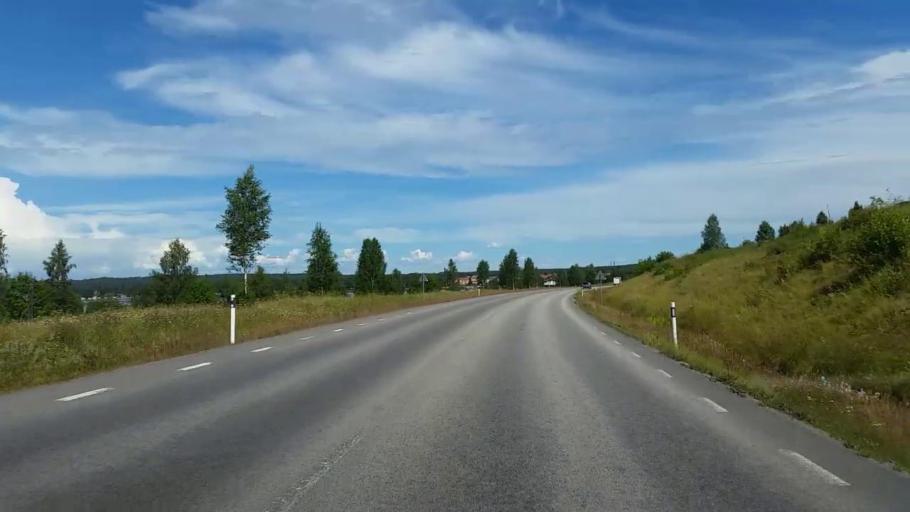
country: SE
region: Dalarna
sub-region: Rattviks Kommun
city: Raettvik
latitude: 60.8733
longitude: 15.1042
